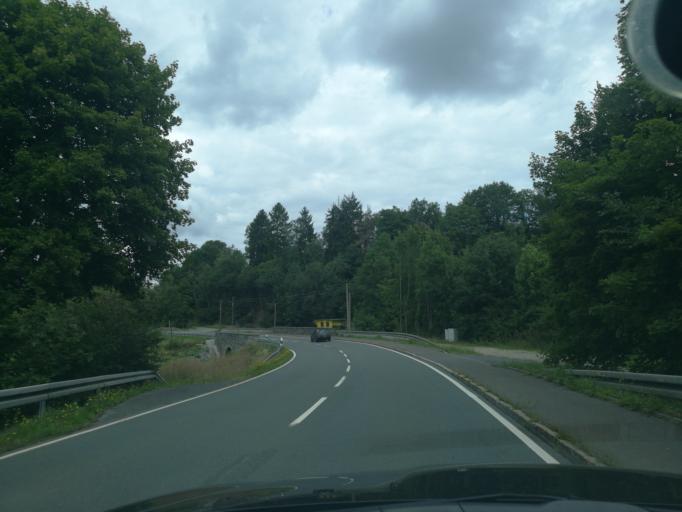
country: DE
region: Saxony
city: Adorf
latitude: 50.3515
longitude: 12.2299
